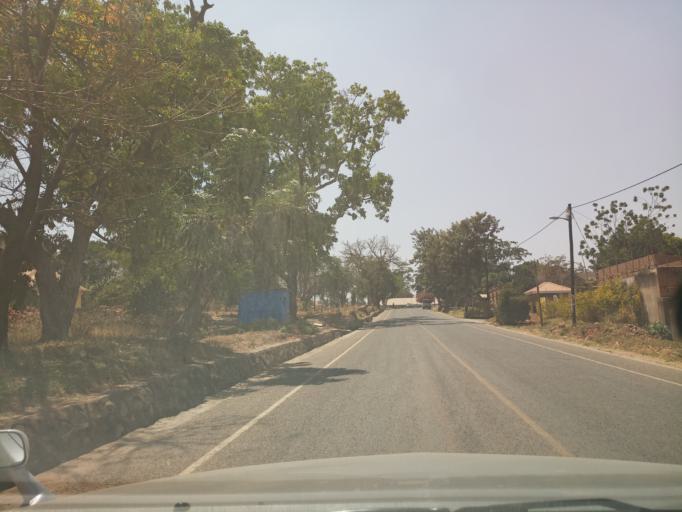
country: UG
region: Northern Region
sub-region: Arua District
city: Arua
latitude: 3.0177
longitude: 30.9148
